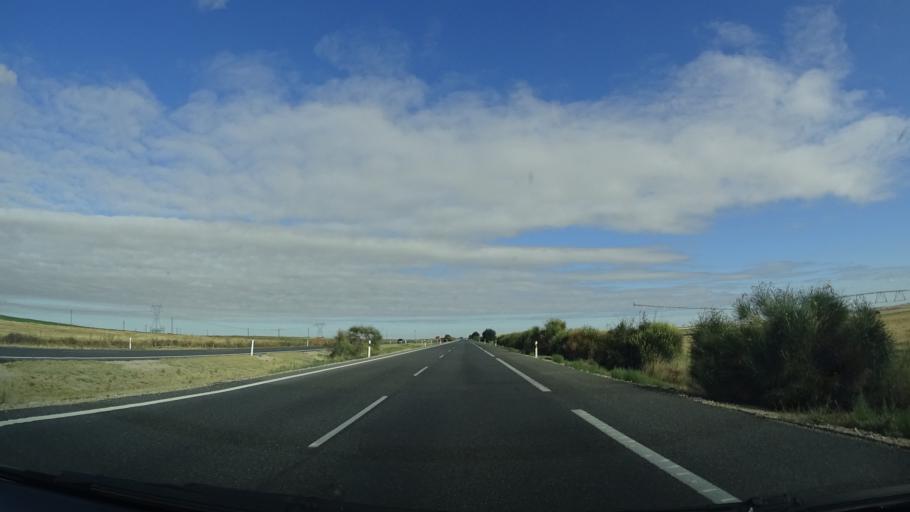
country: ES
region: Castille and Leon
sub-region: Provincia de Valladolid
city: Ataquines
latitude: 41.1931
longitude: -4.8150
